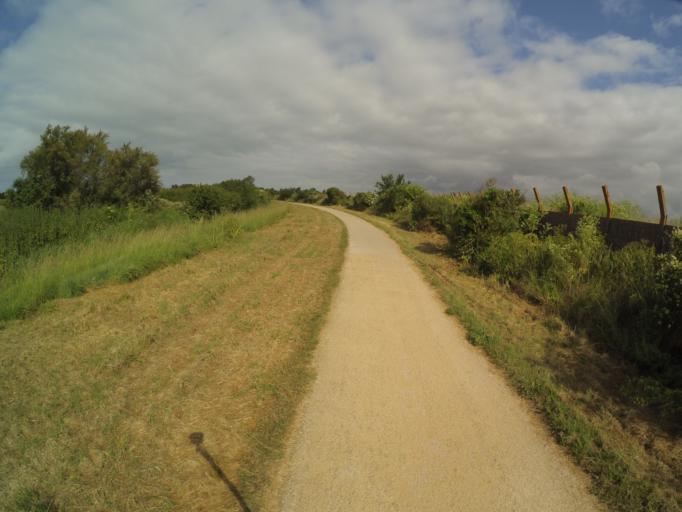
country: FR
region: Poitou-Charentes
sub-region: Departement de la Charente-Maritime
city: Angoulins
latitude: 46.1098
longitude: -1.1184
